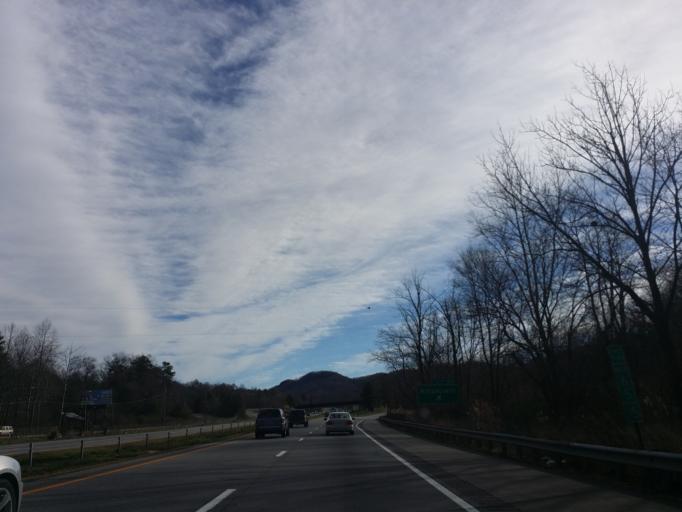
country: US
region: North Carolina
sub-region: Buncombe County
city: Black Mountain
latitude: 35.6191
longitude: -82.2930
